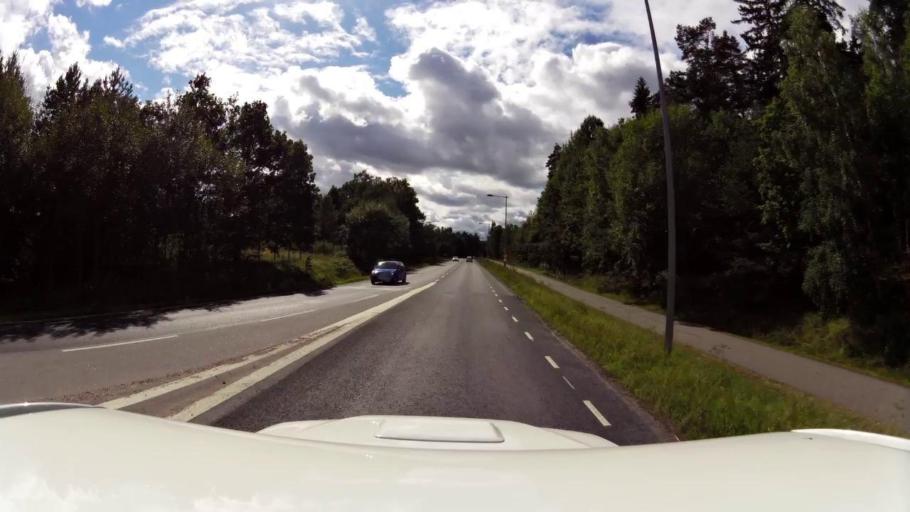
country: SE
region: OEstergoetland
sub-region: Linkopings Kommun
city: Linkoping
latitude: 58.3965
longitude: 15.6051
